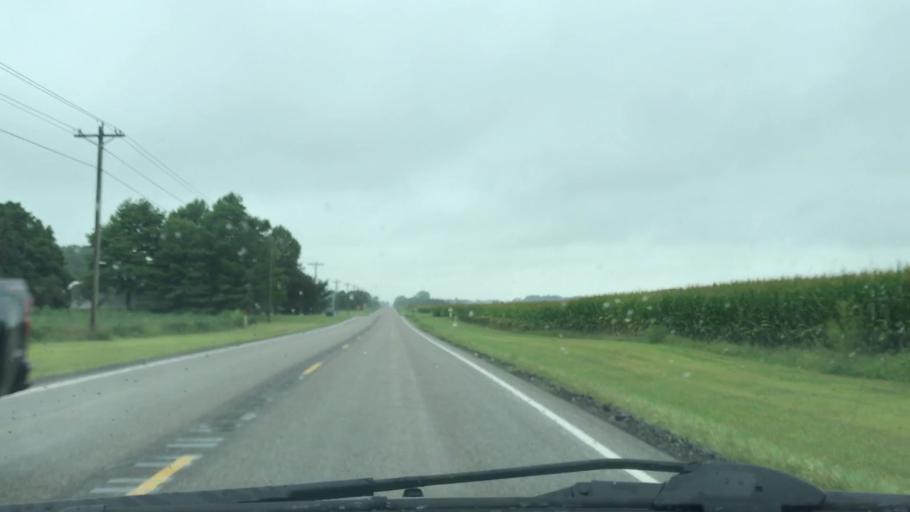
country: US
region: Indiana
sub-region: Boone County
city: Lebanon
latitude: 40.1265
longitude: -86.4177
